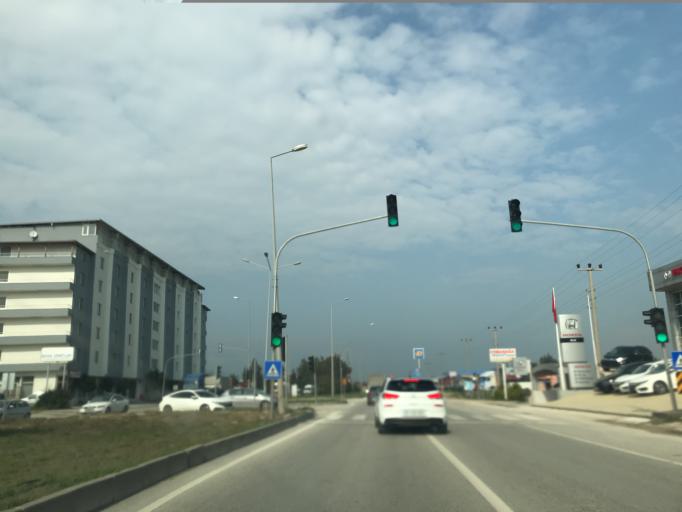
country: TR
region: Hatay
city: Buyuk Dalyan
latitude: 36.2726
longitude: 36.1879
